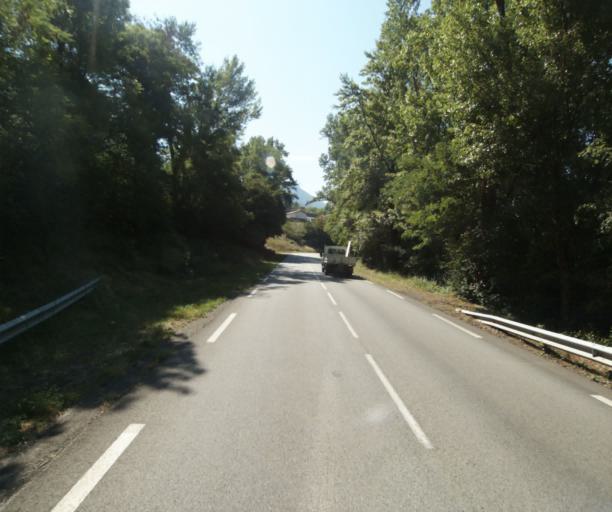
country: FR
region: Rhone-Alpes
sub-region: Departement de l'Isere
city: Saint-Georges-de-Commiers
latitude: 45.0490
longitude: 5.7091
